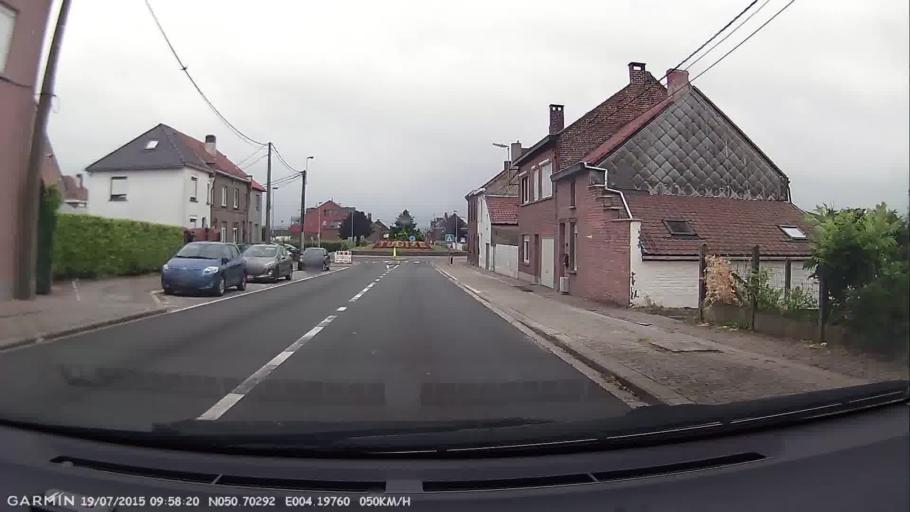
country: BE
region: Wallonia
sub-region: Province du Brabant Wallon
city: Tubize
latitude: 50.7028
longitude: 4.1977
